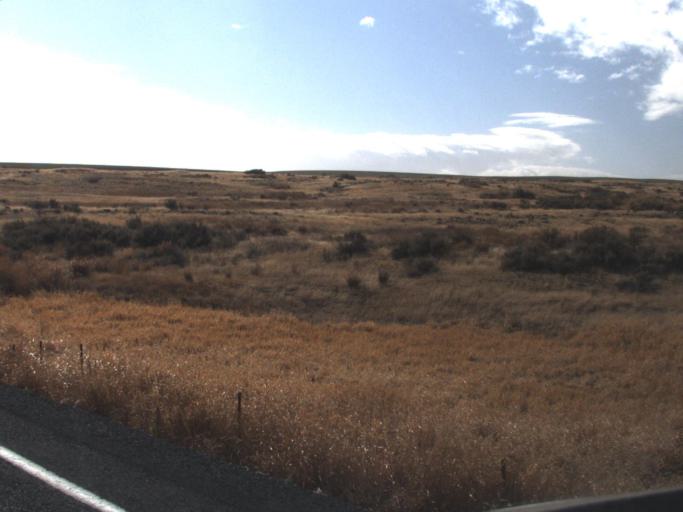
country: US
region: Washington
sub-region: Okanogan County
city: Coulee Dam
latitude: 47.6654
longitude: -118.7215
